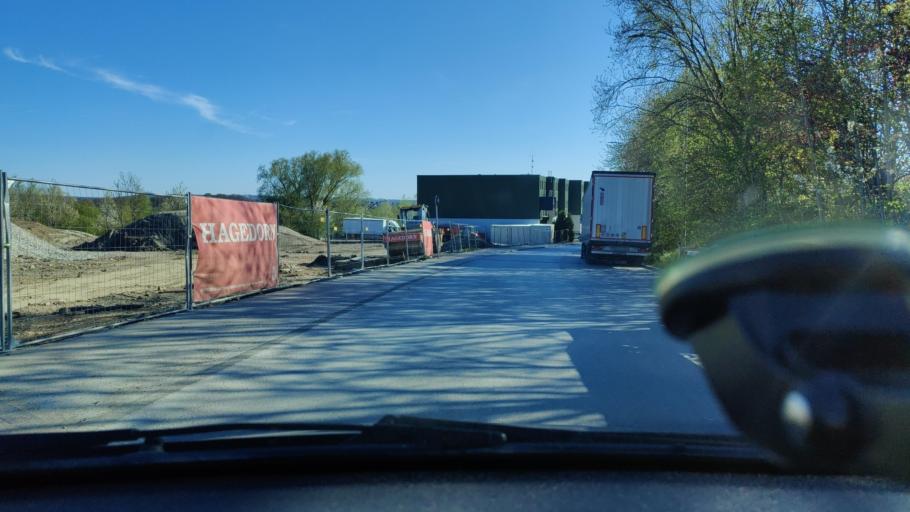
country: DE
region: North Rhine-Westphalia
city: Wulfrath
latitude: 51.2951
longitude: 7.0580
